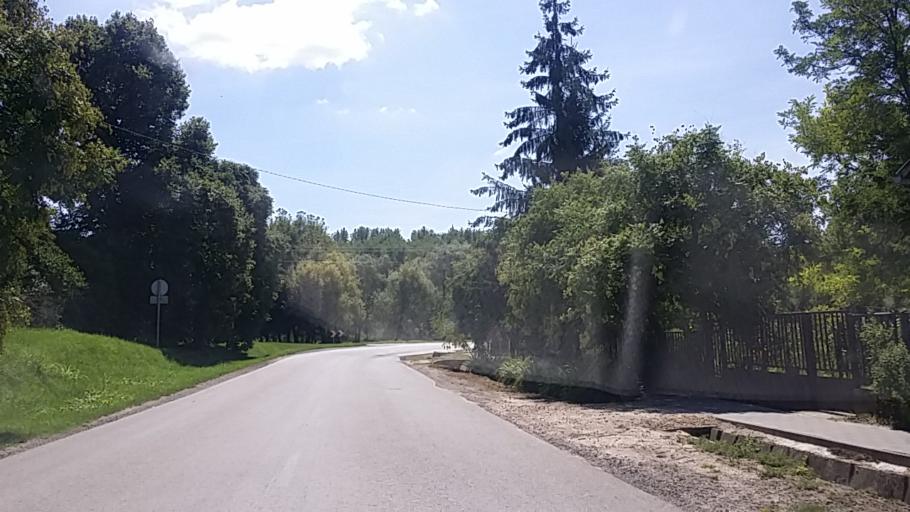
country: HU
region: Fejer
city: Deg
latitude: 46.8662
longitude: 18.4439
